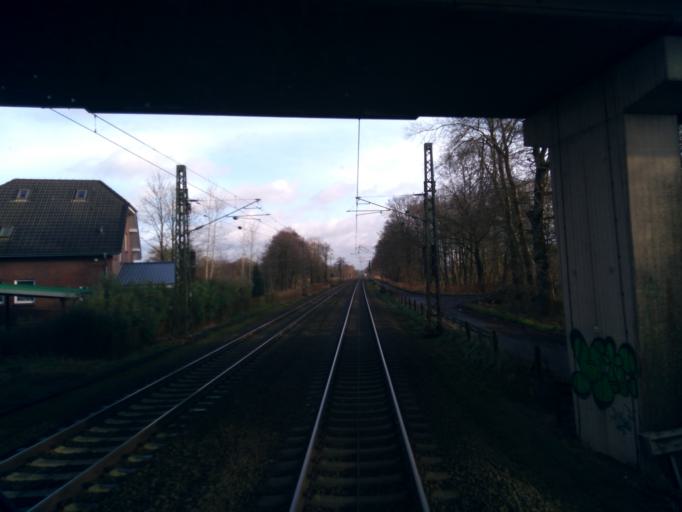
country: DE
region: Lower Saxony
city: Hassendorf
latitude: 53.1016
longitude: 9.2663
